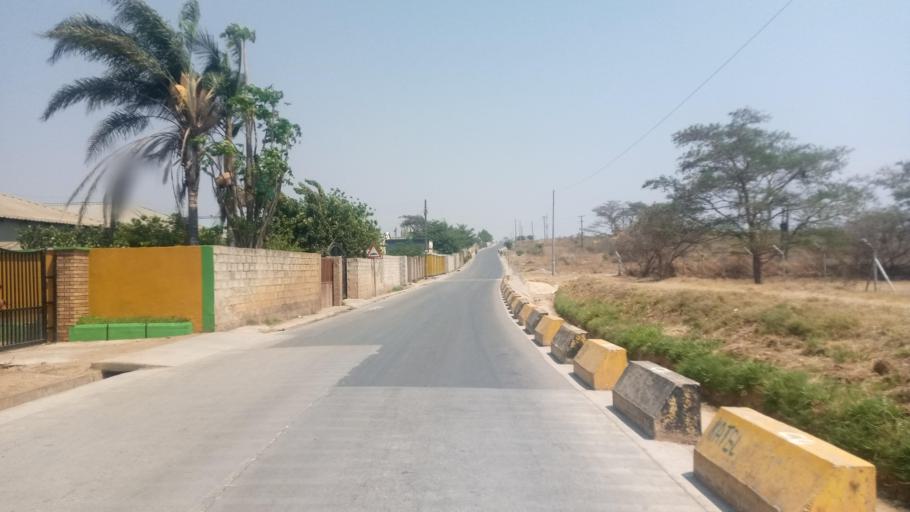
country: ZM
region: Lusaka
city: Lusaka
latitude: -15.4362
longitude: 28.3799
